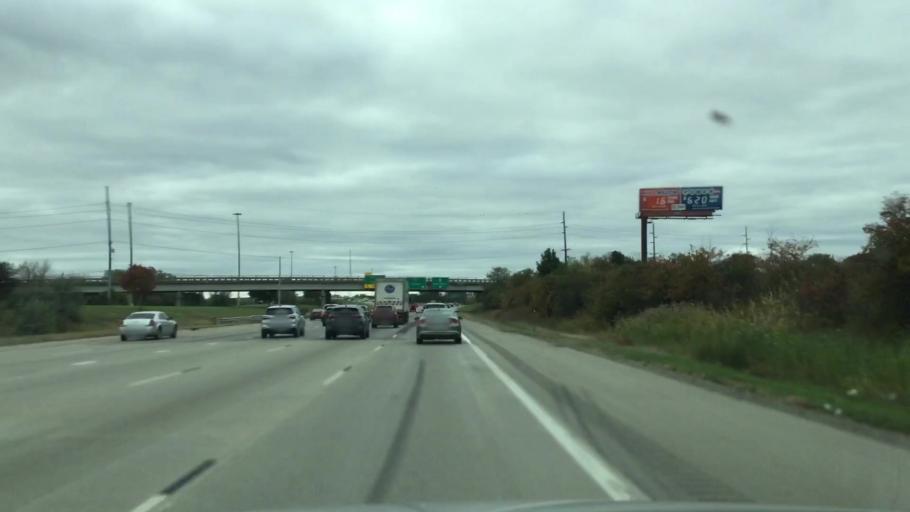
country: US
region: Michigan
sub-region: Wayne County
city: Plymouth
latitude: 42.3980
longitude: -83.4309
